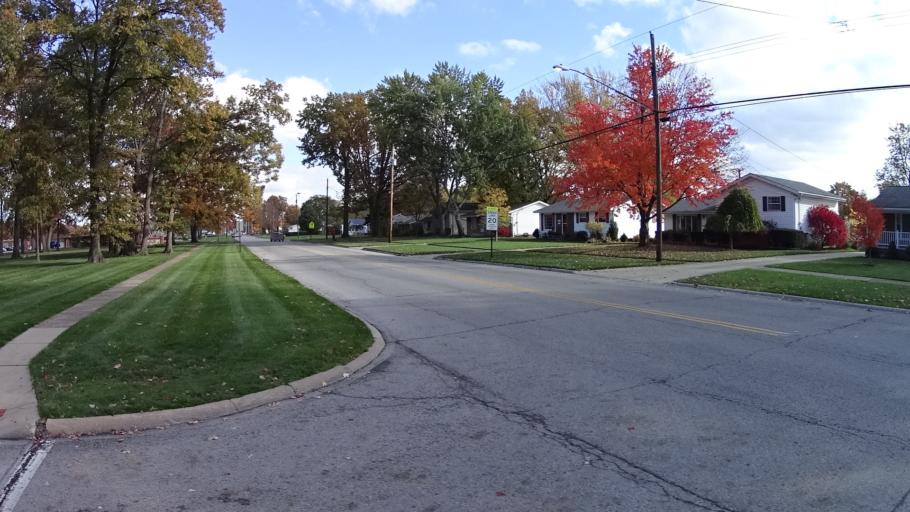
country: US
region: Ohio
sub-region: Lorain County
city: Sheffield
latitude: 41.4360
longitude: -82.1237
